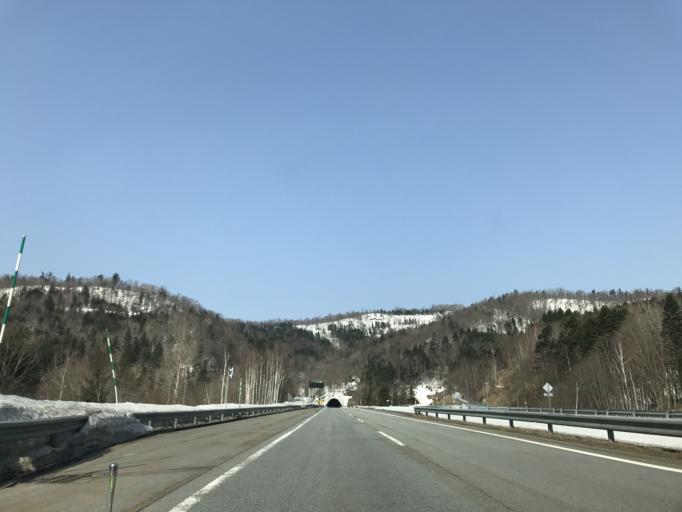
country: JP
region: Hokkaido
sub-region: Asahikawa-shi
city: Asahikawa
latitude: 43.7921
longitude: 142.2698
